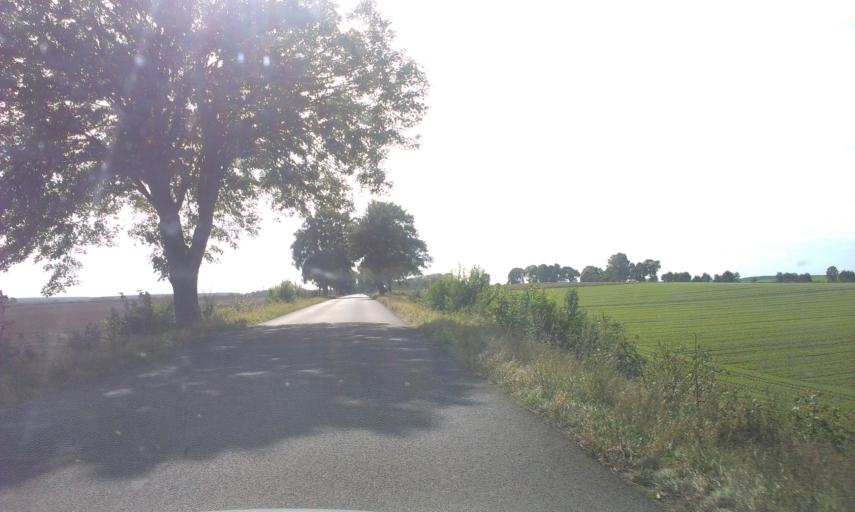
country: PL
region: Greater Poland Voivodeship
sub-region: Powiat zlotowski
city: Zlotow
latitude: 53.4614
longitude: 16.9875
